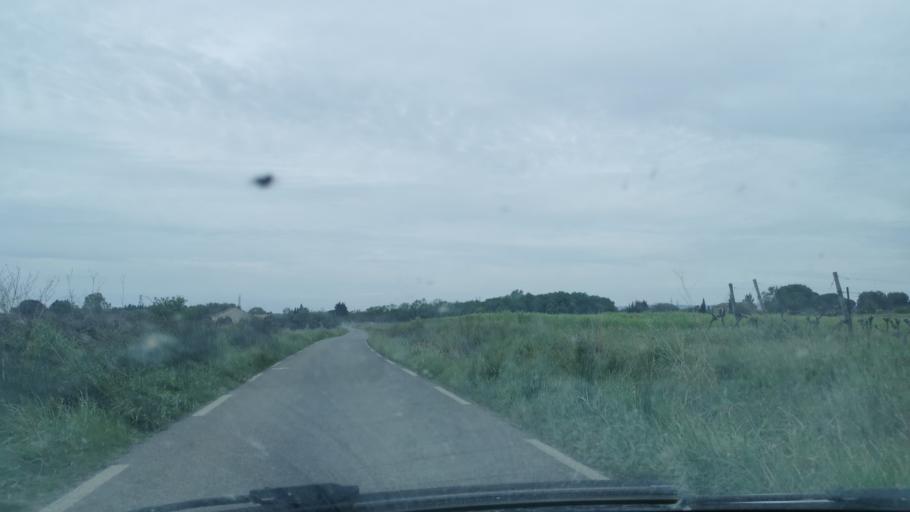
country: FR
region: Languedoc-Roussillon
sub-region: Departement de l'Herault
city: Fabregues
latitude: 43.5603
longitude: 3.7698
